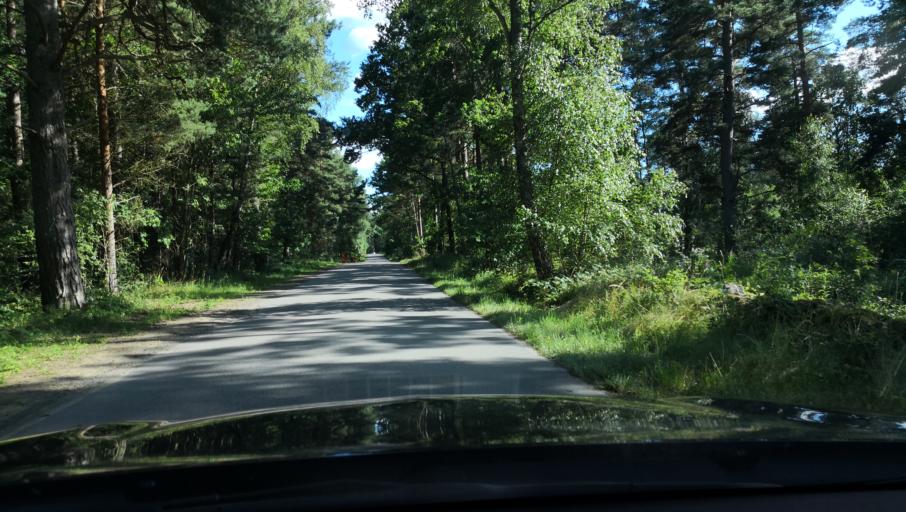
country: SE
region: Skane
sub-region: Simrishamns Kommun
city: Kivik
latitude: 55.7809
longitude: 14.1938
